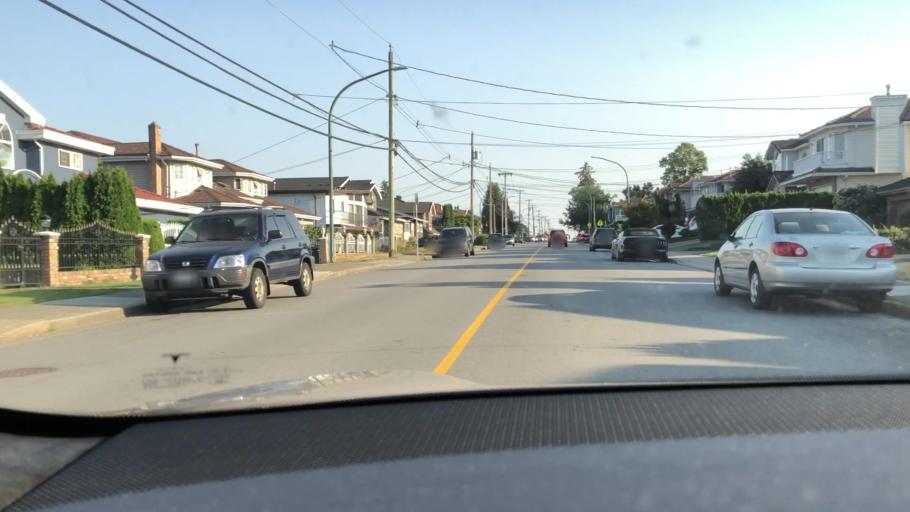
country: CA
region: British Columbia
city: Burnaby
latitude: 49.2235
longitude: -122.9720
